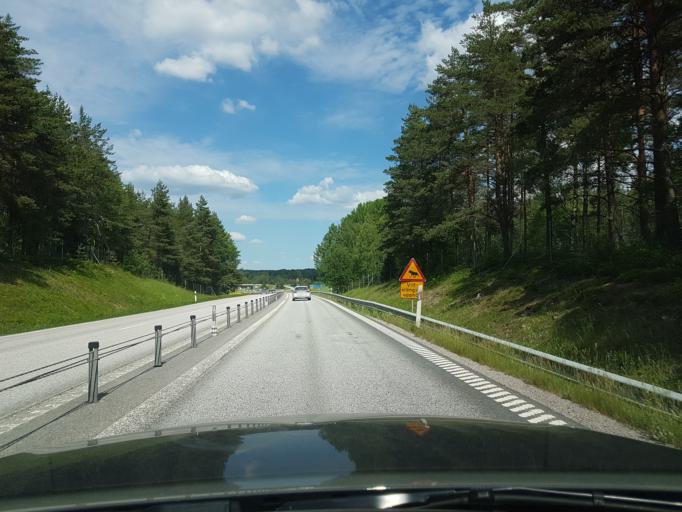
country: SE
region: Stockholm
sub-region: Osterakers Kommun
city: Akersberga
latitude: 59.5535
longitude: 18.2298
